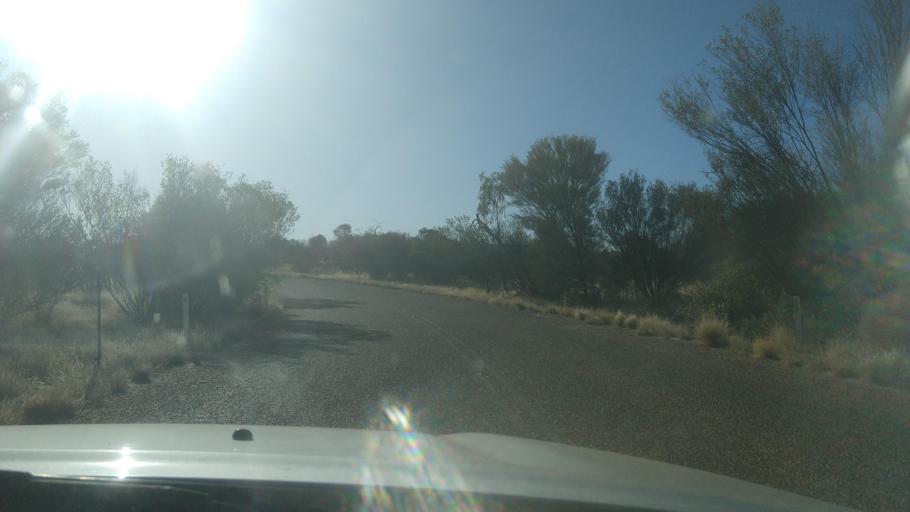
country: AU
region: Northern Territory
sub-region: Alice Springs
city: Alice Springs
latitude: -23.7031
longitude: 133.8335
